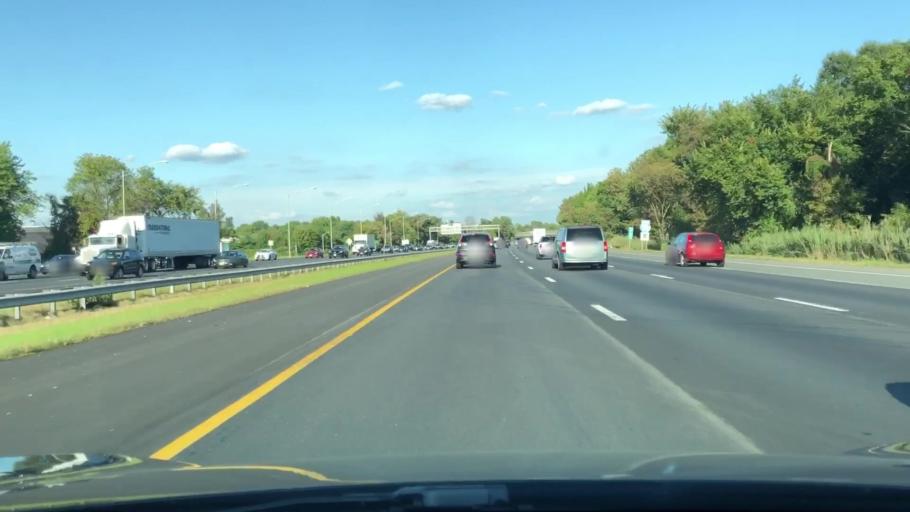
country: US
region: New Jersey
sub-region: Burlington County
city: Ramblewood
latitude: 39.9370
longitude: -74.9615
